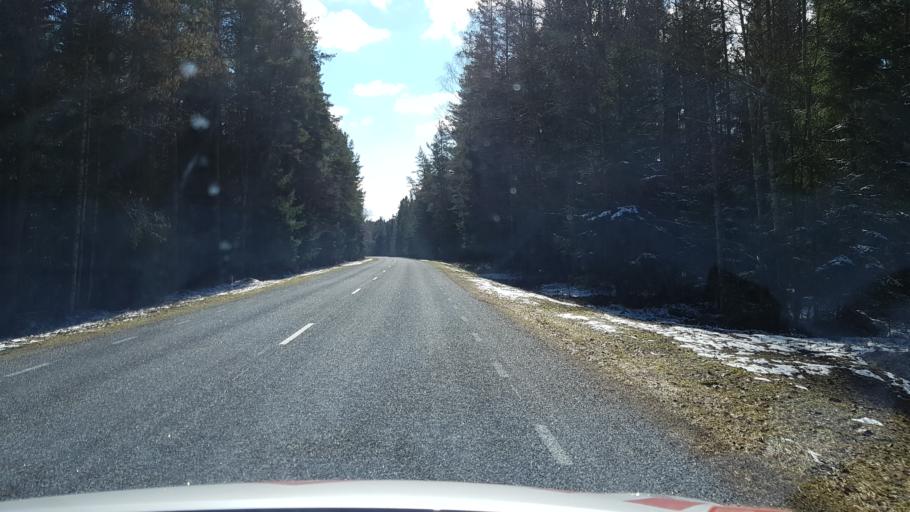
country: EE
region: Harju
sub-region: Loksa linn
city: Loksa
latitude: 59.5709
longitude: 25.9339
